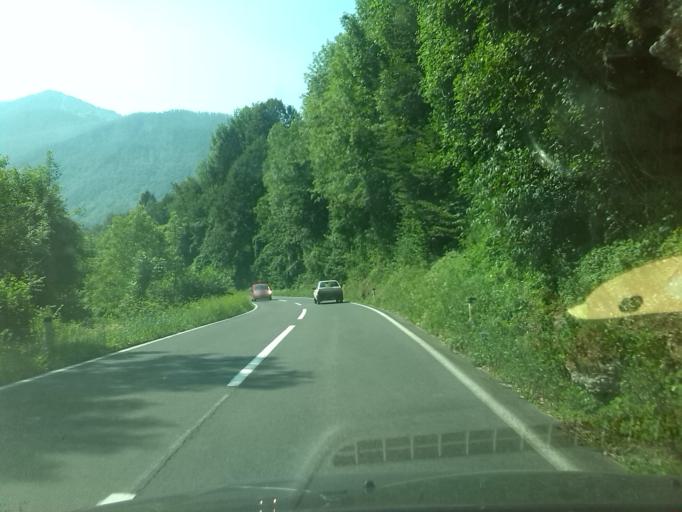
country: SI
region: Kobarid
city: Kobarid
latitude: 46.2289
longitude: 13.5956
